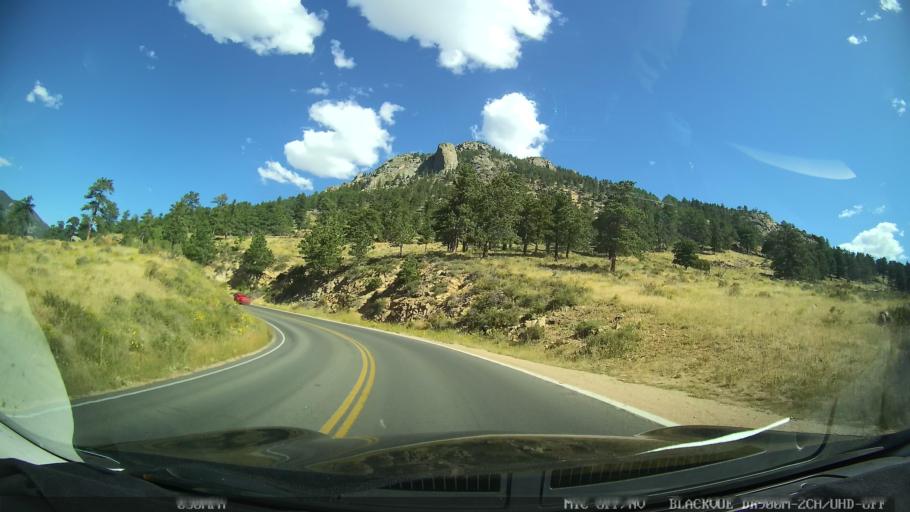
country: US
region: Colorado
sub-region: Larimer County
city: Estes Park
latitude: 40.3693
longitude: -105.5864
